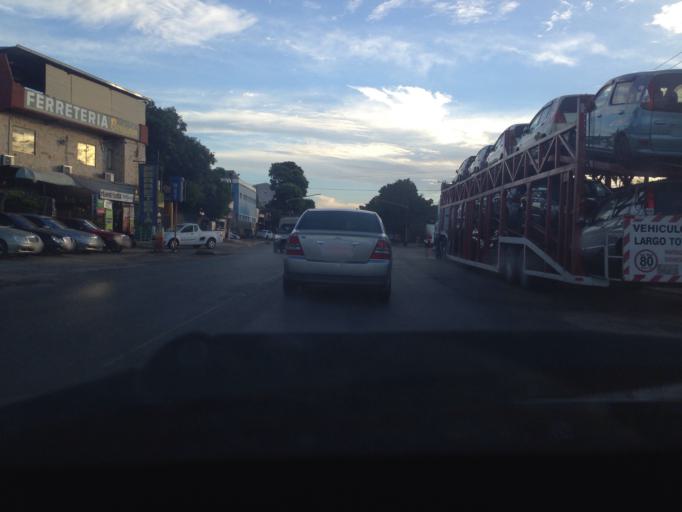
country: PY
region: Central
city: Lambare
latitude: -25.3447
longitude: -57.5880
